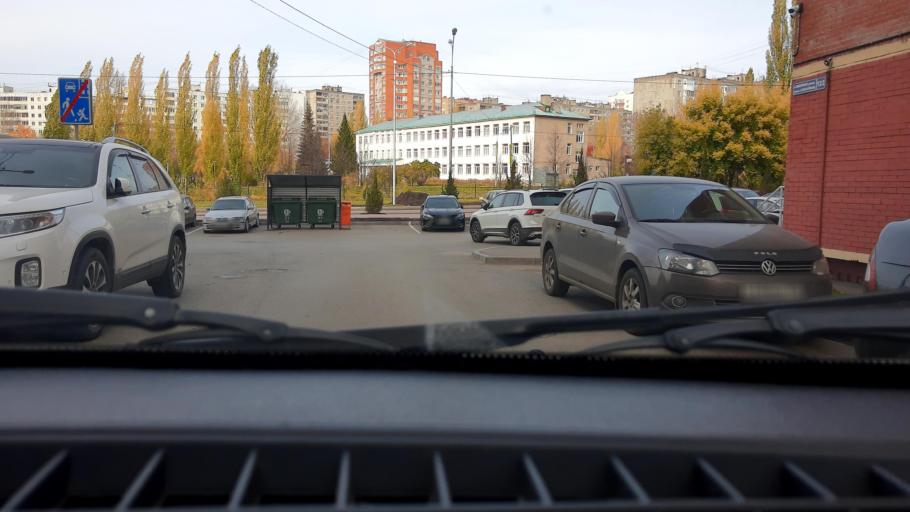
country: RU
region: Bashkortostan
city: Ufa
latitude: 54.6976
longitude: 55.9972
